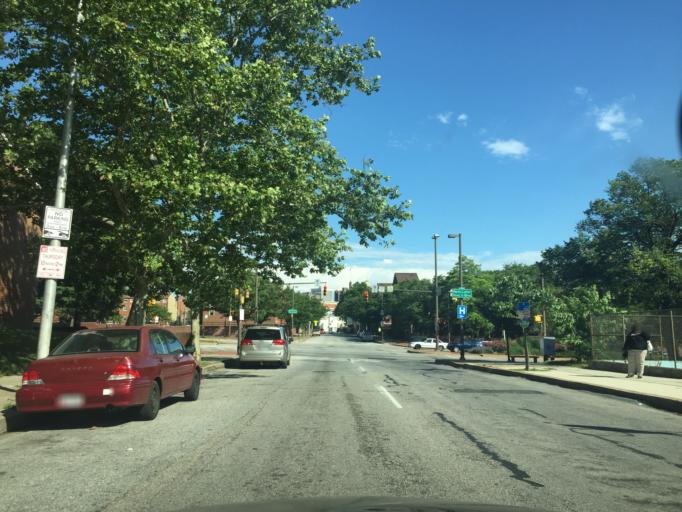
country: US
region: Maryland
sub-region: City of Baltimore
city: Baltimore
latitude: 39.2989
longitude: -76.6247
